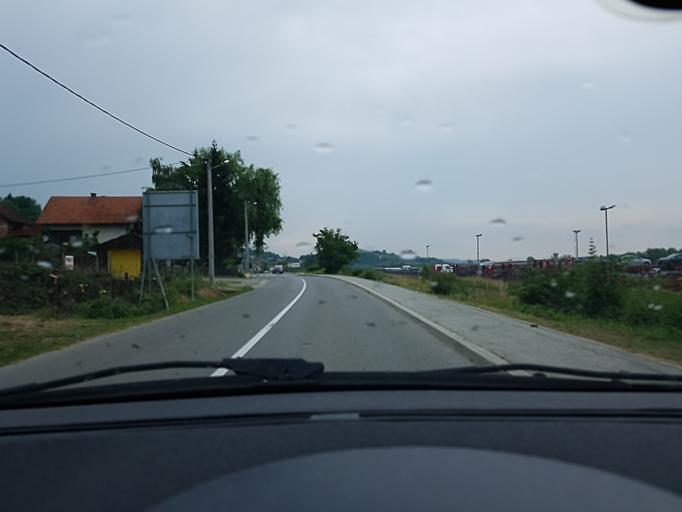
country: HR
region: Zagrebacka
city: Pojatno
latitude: 45.9117
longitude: 15.8083
